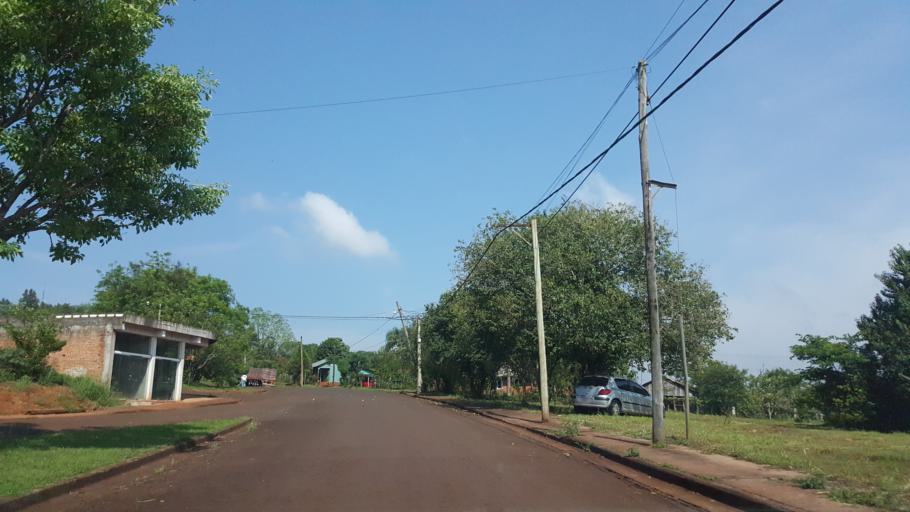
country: AR
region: Misiones
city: Capiovi
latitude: -26.9289
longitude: -55.0633
